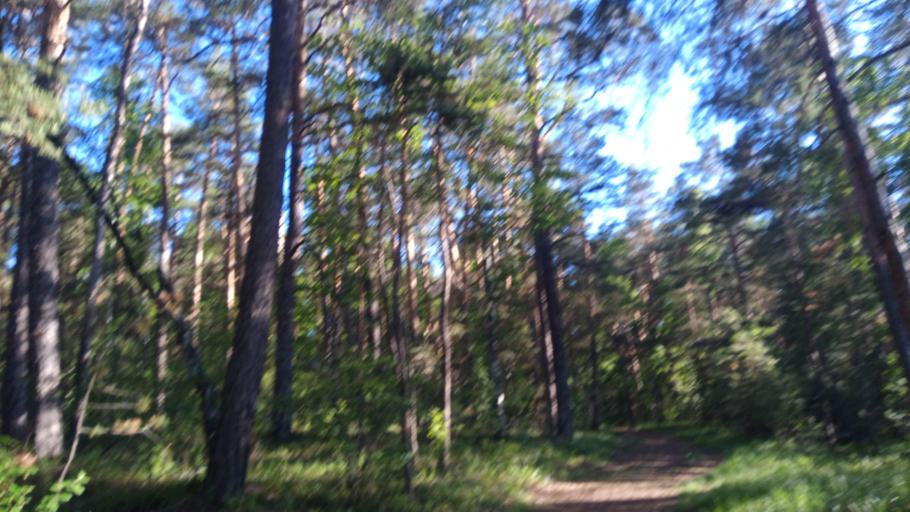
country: RU
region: Chelyabinsk
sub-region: Gorod Chelyabinsk
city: Chelyabinsk
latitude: 55.1316
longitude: 61.3353
